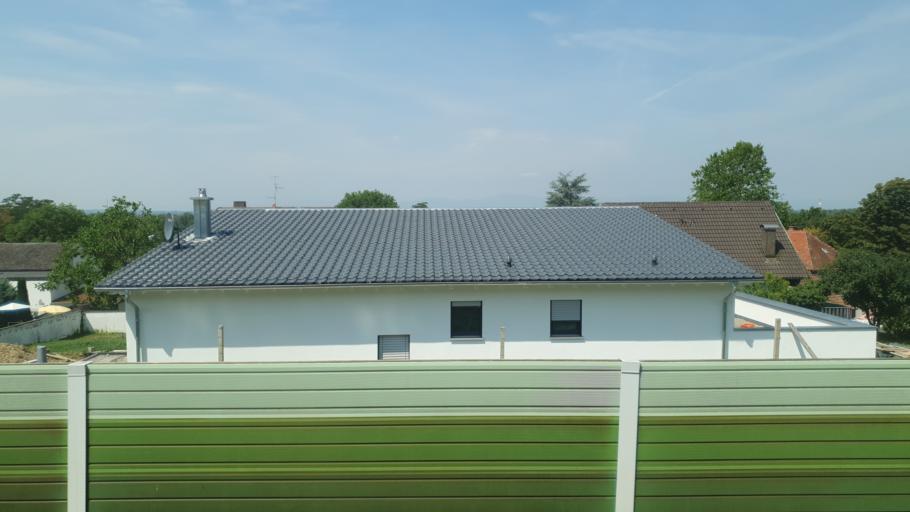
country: DE
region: Baden-Wuerttemberg
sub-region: Freiburg Region
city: Bad Bellingen
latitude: 47.7288
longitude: 7.5565
